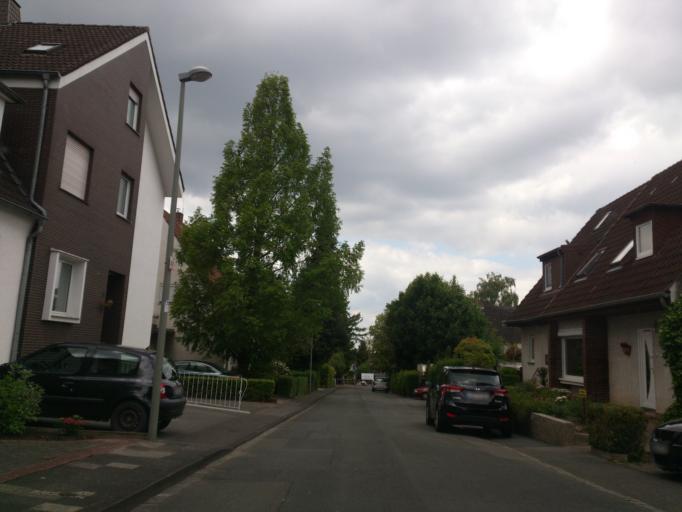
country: DE
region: North Rhine-Westphalia
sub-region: Regierungsbezirk Detmold
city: Paderborn
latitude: 51.7141
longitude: 8.7729
